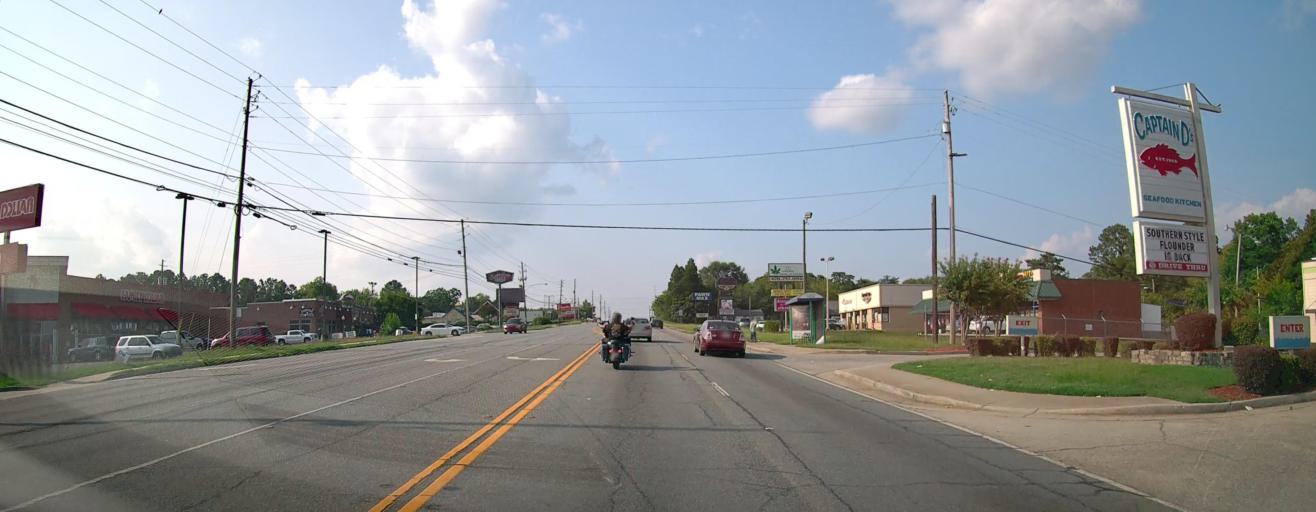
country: US
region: Georgia
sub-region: Bibb County
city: Macon
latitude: 32.8151
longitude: -83.6628
